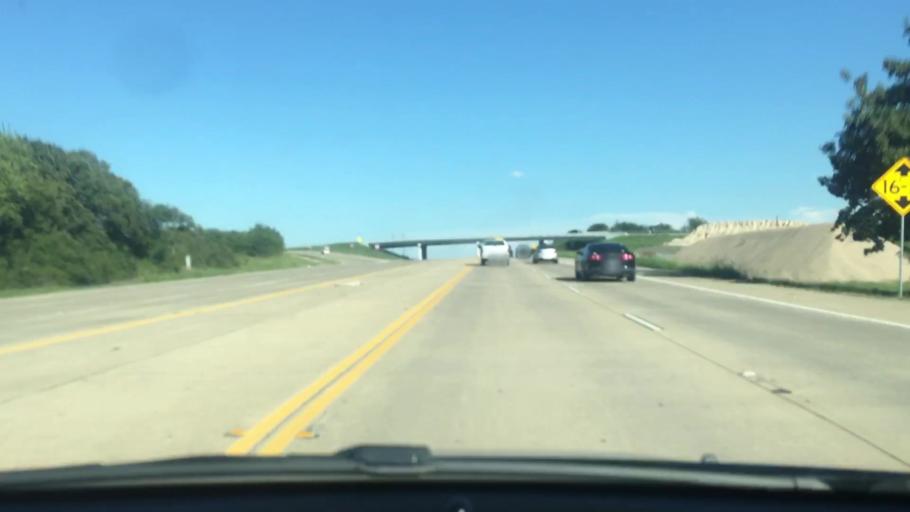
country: US
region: Texas
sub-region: Denton County
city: Cross Roads
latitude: 33.2324
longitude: -97.0085
